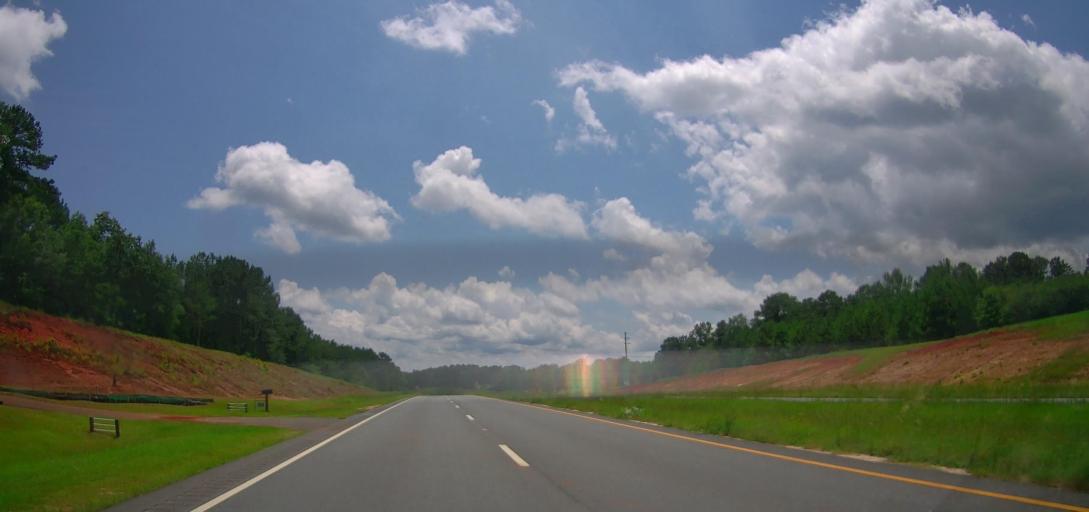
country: US
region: Georgia
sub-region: Upson County
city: Thomaston
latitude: 32.8332
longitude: -84.3086
